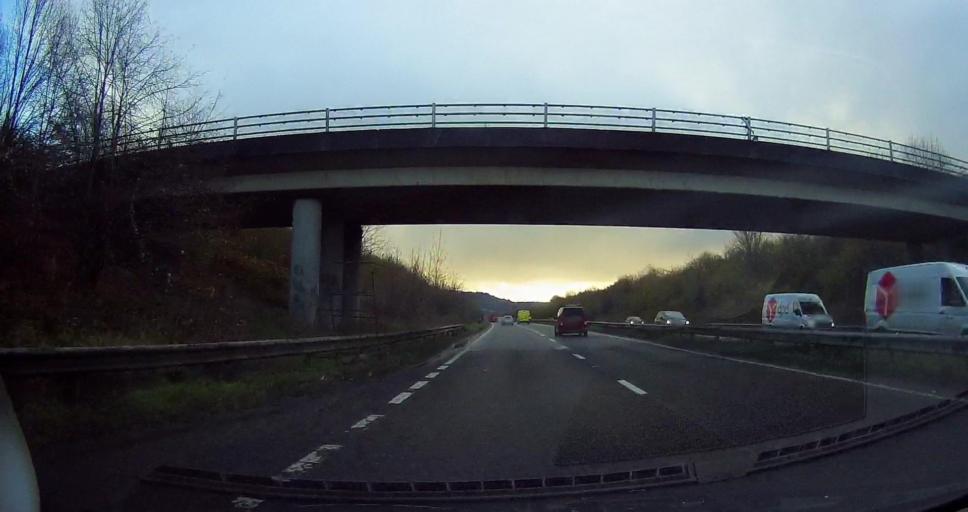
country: GB
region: England
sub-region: West Sussex
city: Hurstpierpoint
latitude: 50.9356
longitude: -0.1954
